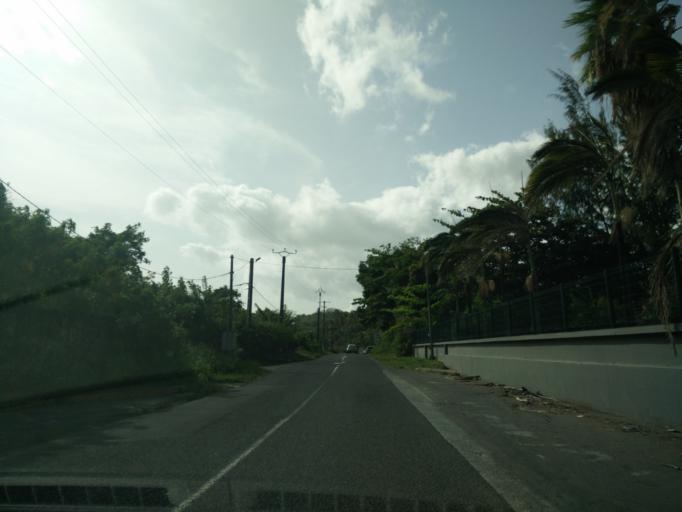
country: MQ
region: Martinique
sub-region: Martinique
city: Saint-Pierre
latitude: 14.7557
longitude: -61.1834
